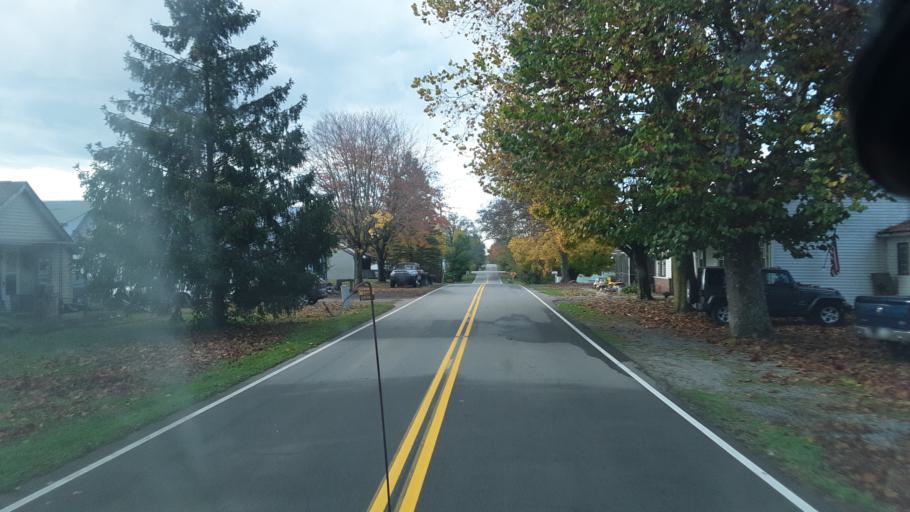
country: US
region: Ohio
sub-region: Highland County
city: Greenfield
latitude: 39.3987
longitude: -83.4628
